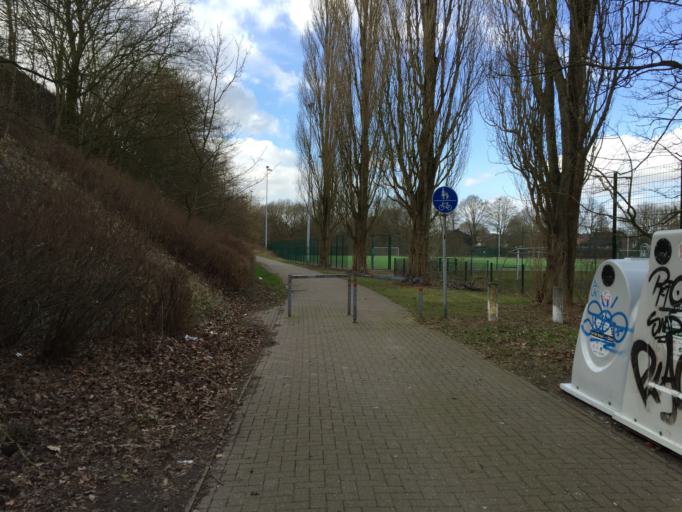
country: DE
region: Lower Saxony
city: Oldenburg
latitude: 53.1624
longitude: 8.2321
